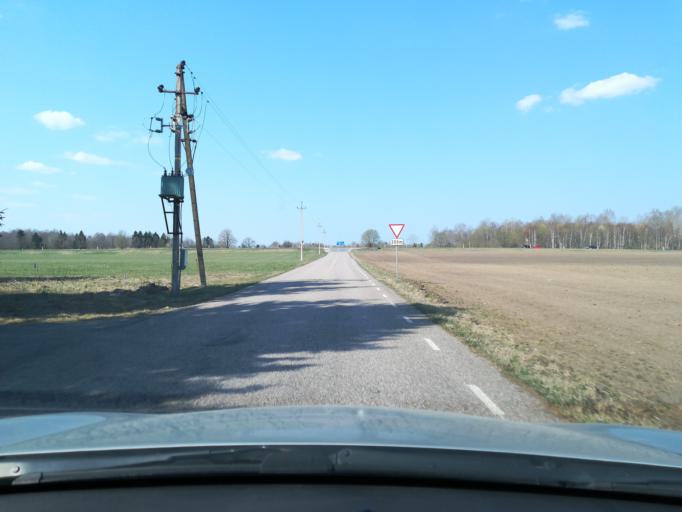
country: EE
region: Harju
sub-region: Saue linn
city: Saue
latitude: 59.3353
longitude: 24.4830
